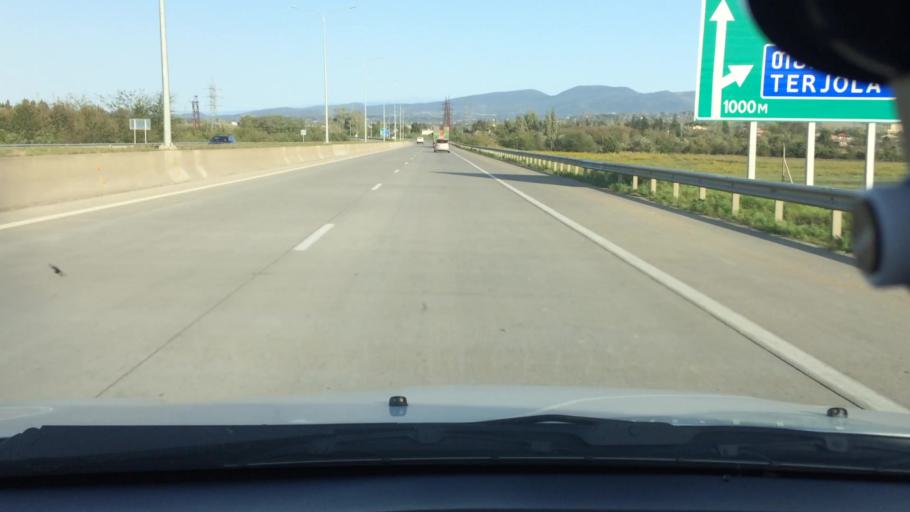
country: GE
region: Imereti
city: Zestap'oni
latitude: 42.1511
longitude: 42.9604
